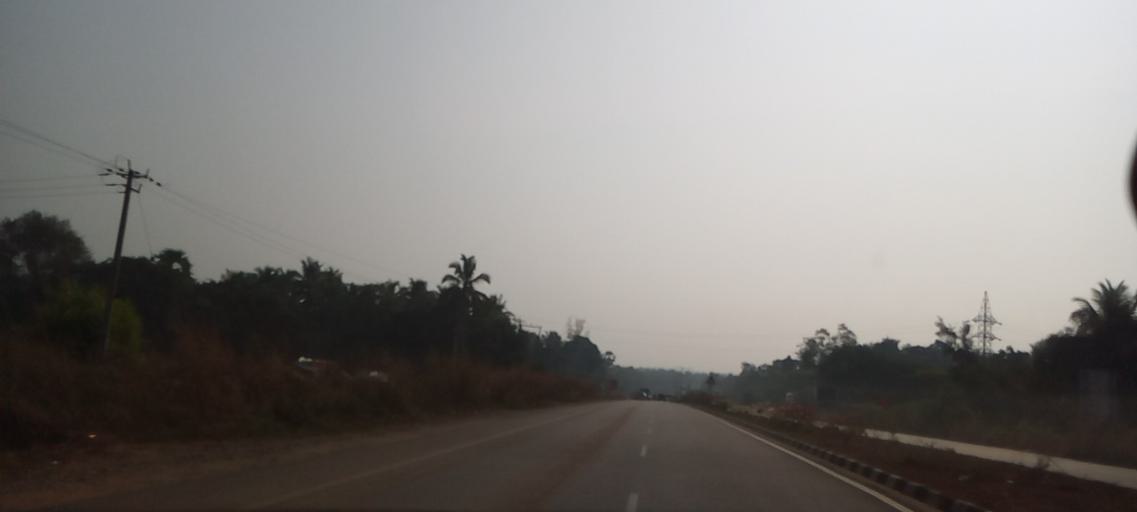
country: IN
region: Karnataka
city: Gangolli
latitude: 13.6887
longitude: 74.6722
